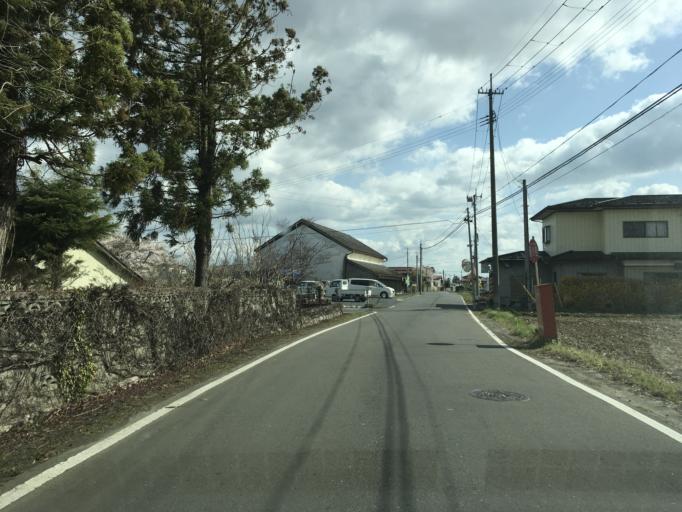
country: JP
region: Iwate
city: Ichinoseki
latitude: 38.7423
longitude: 141.2663
